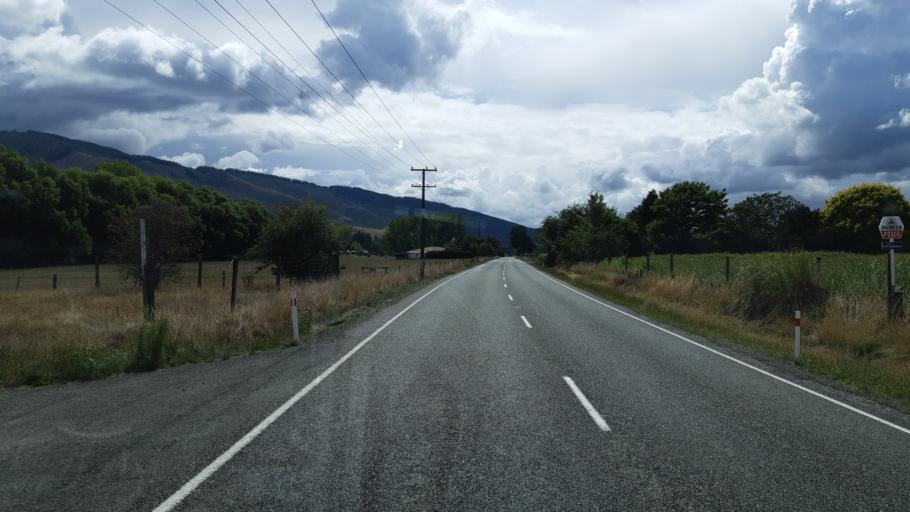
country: NZ
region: Tasman
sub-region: Tasman District
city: Wakefield
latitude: -41.4713
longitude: 172.8065
